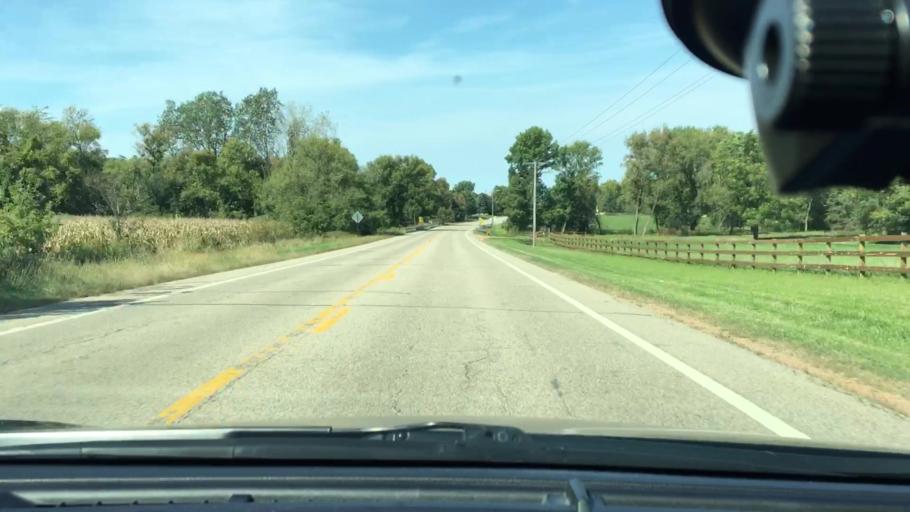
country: US
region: Minnesota
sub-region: Hennepin County
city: Corcoran
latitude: 45.1007
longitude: -93.5556
